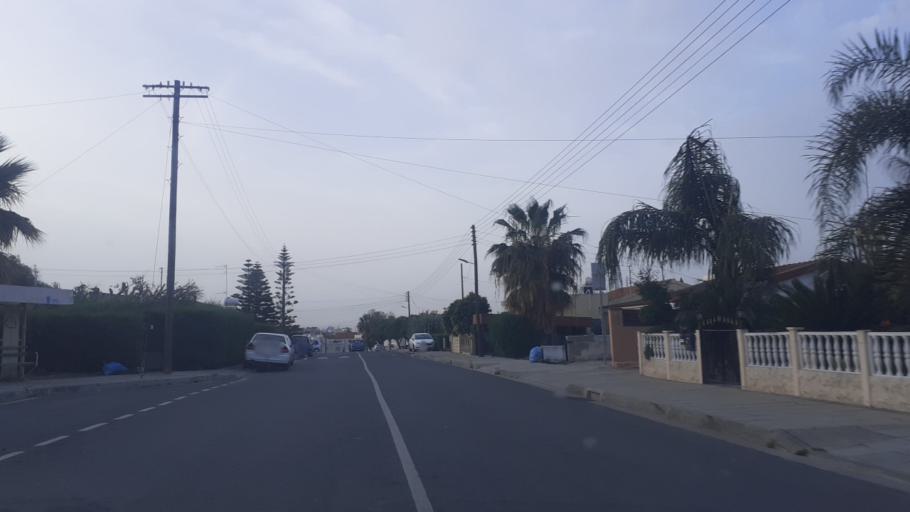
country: CY
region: Larnaka
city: Kolossi
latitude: 34.6591
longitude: 32.9564
